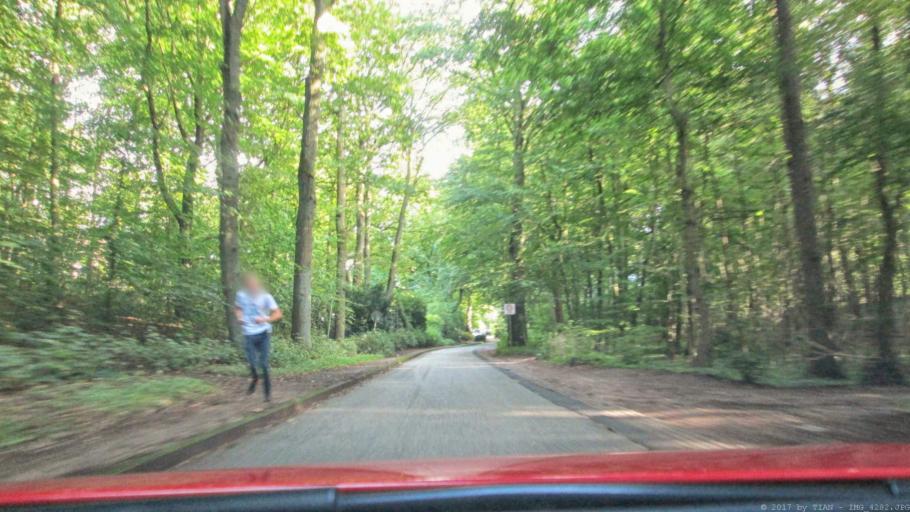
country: DE
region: Schleswig-Holstein
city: Rellingen
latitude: 53.5731
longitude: 9.7891
